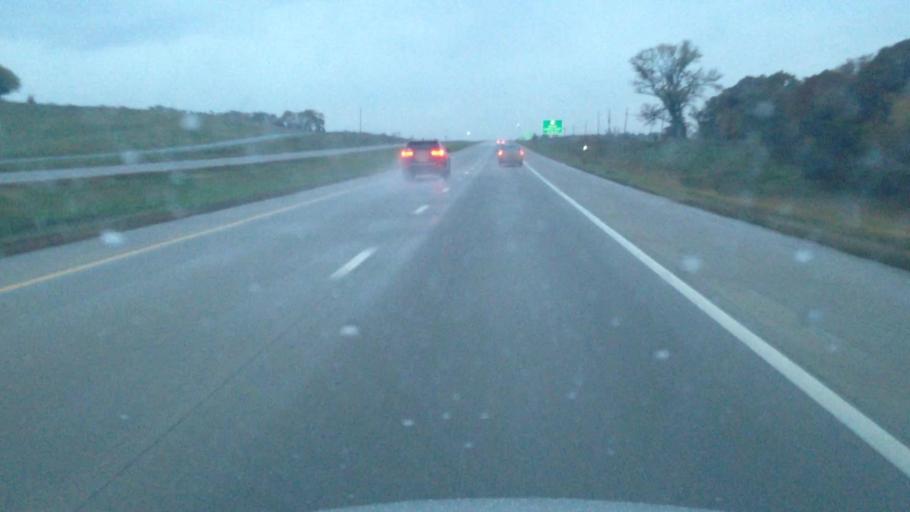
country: US
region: Kansas
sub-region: Douglas County
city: Baldwin City
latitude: 38.7980
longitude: -95.2693
